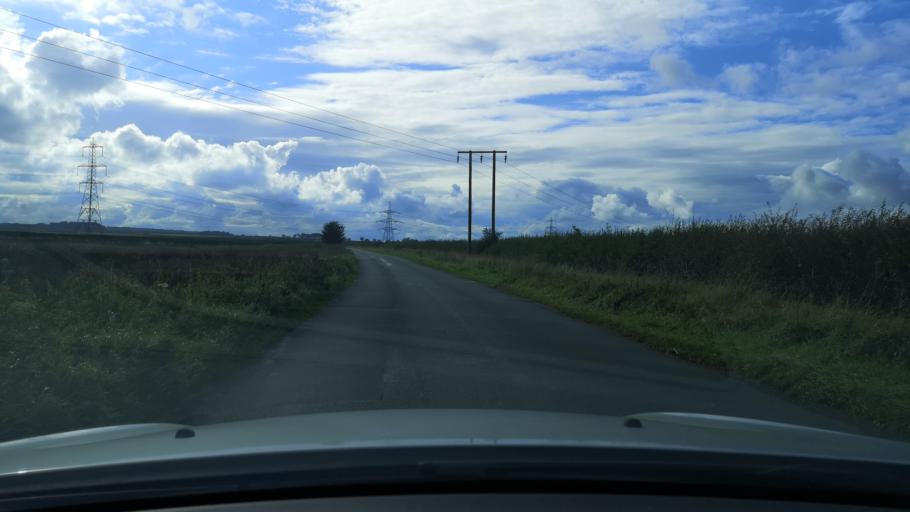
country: GB
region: England
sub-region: East Riding of Yorkshire
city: Walkington
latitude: 53.8312
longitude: -0.4987
